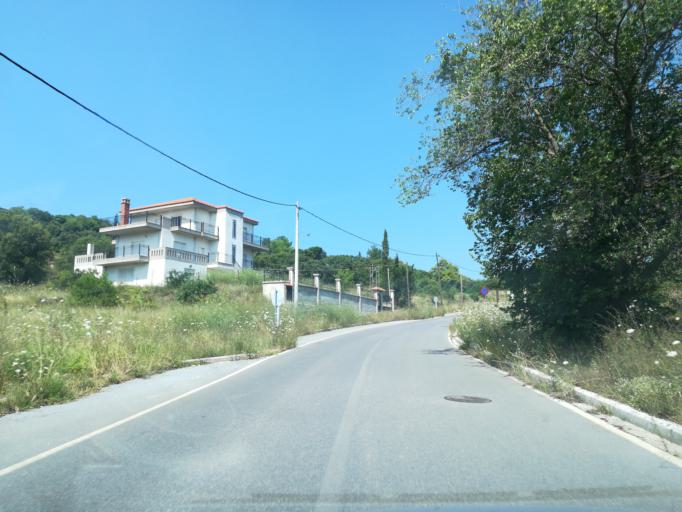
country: GR
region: Central Macedonia
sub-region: Nomos Thessalonikis
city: Asvestochori
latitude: 40.6291
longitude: 23.0362
